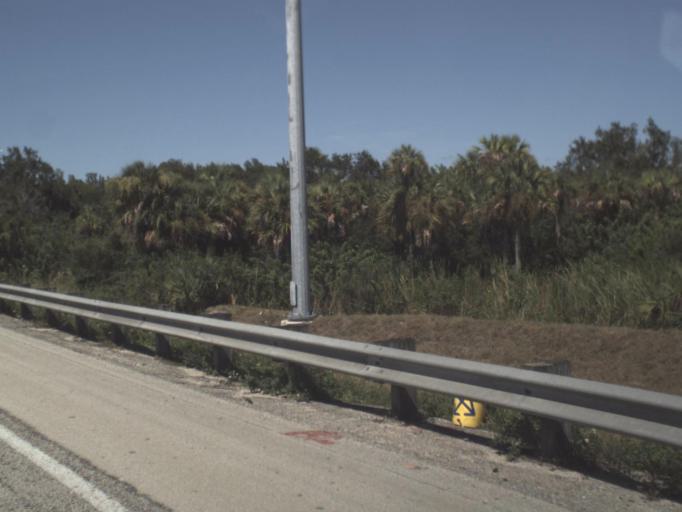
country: US
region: Florida
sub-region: Lee County
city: Tice
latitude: 26.7110
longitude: -81.8083
